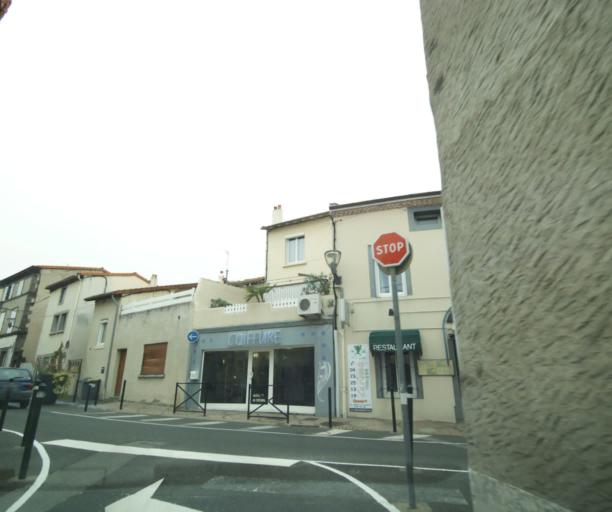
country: FR
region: Auvergne
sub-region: Departement du Puy-de-Dome
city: Gerzat
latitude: 45.8238
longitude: 3.1450
